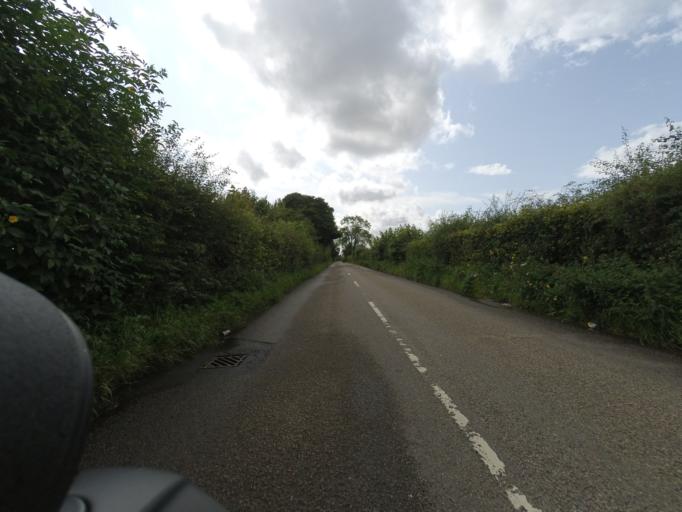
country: GB
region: Scotland
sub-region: Highland
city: Tain
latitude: 57.7432
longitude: -4.0748
